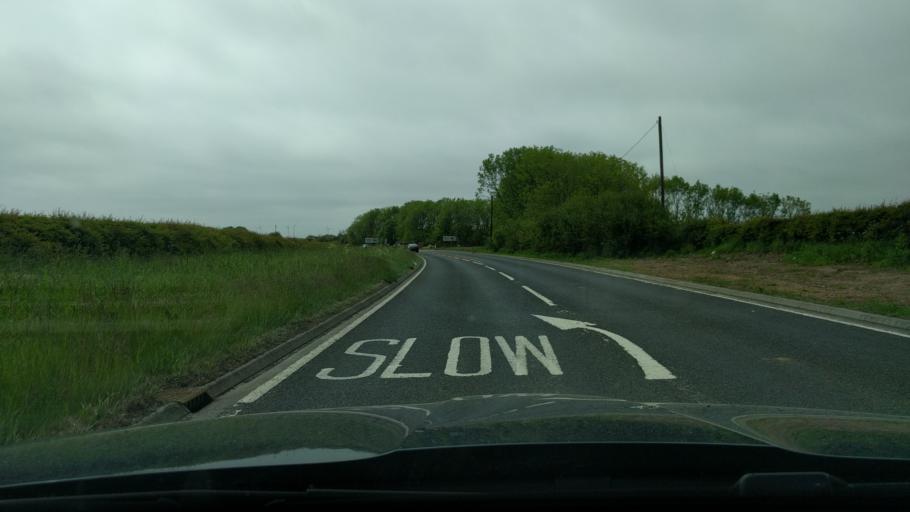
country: GB
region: England
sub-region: Northumberland
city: Cresswell
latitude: 55.2363
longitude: -1.5925
